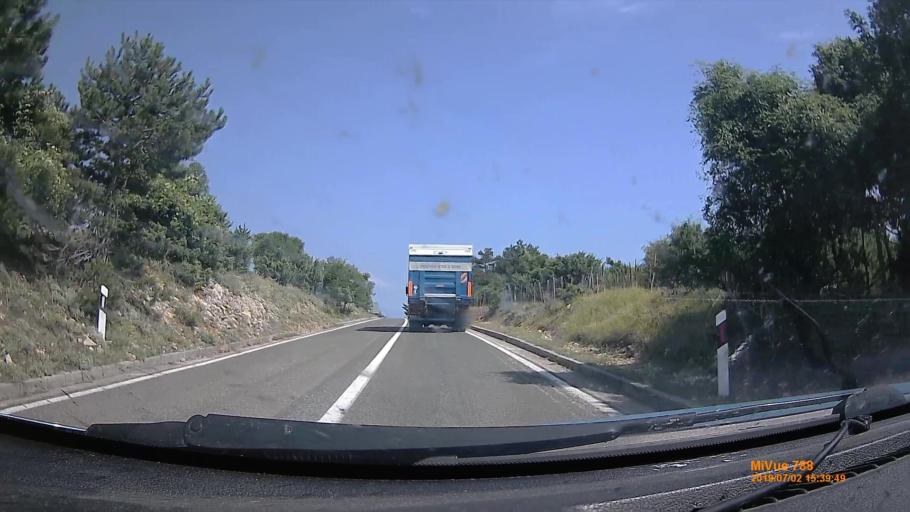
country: HR
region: Primorsko-Goranska
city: Cres
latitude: 44.9706
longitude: 14.4287
